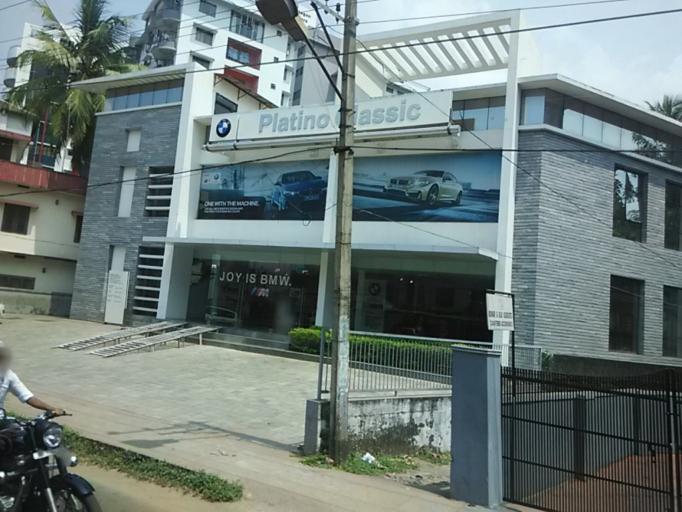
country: IN
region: Kerala
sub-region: Kozhikode
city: Kozhikode
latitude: 11.2742
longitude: 75.7741
